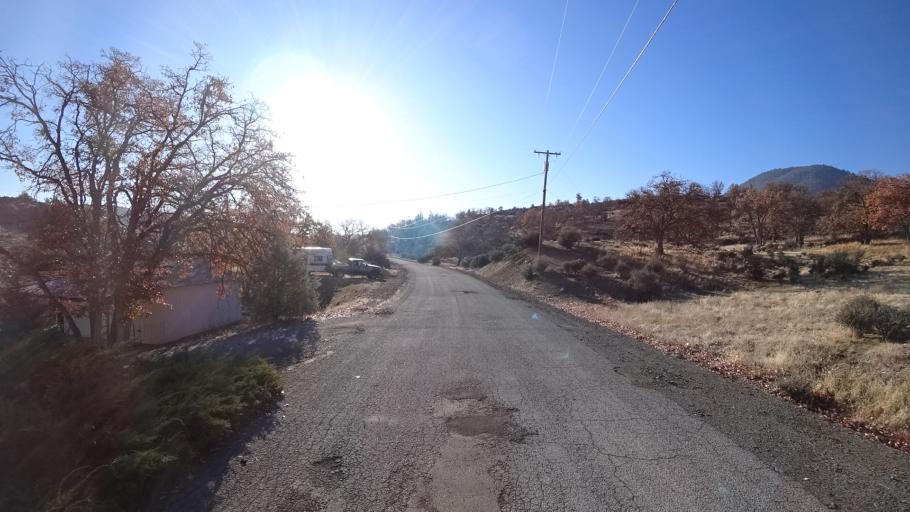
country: US
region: California
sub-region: Siskiyou County
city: Montague
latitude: 41.8936
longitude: -122.4965
